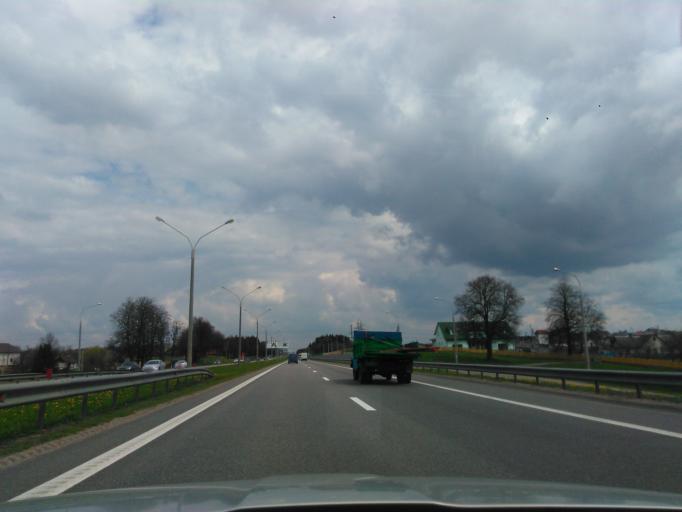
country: BY
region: Minsk
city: Korolev Stan
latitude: 53.9891
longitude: 27.8000
